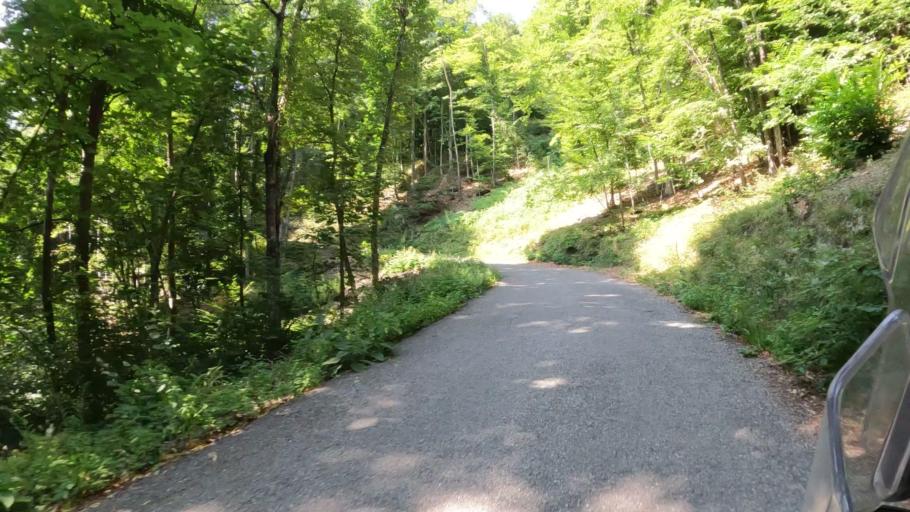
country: IT
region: Piedmont
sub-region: Provincia di Torino
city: Lemie
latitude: 45.2168
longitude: 7.3132
